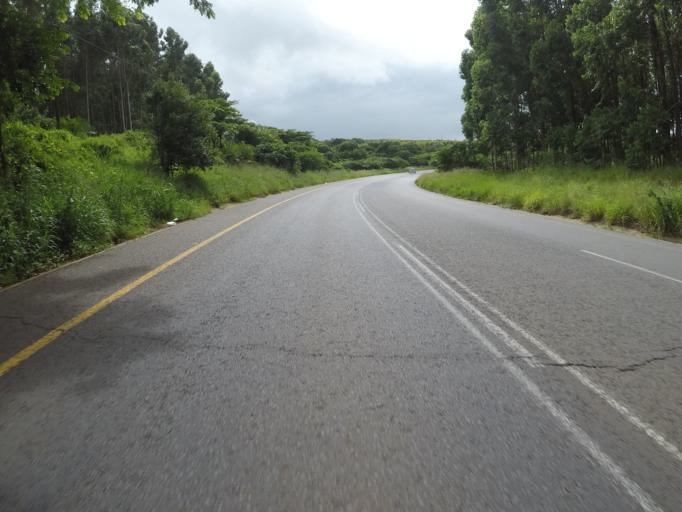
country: ZA
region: KwaZulu-Natal
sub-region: uThungulu District Municipality
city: eSikhawini
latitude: -28.8644
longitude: 31.8919
